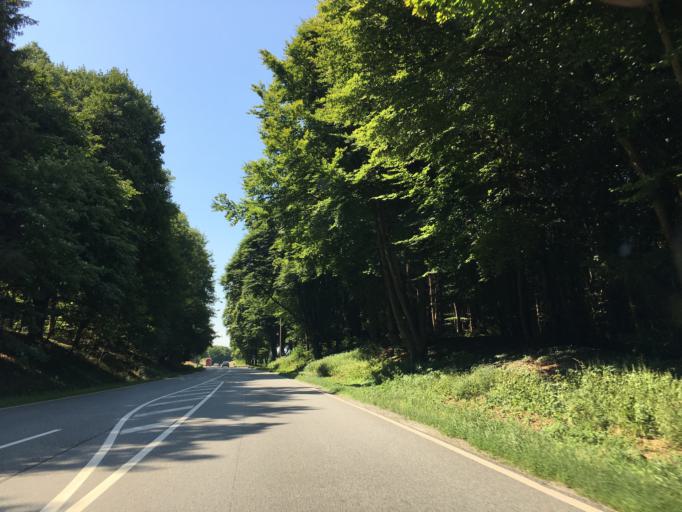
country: DE
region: Bavaria
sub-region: Upper Bavaria
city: Edling
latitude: 48.0462
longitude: 12.1850
